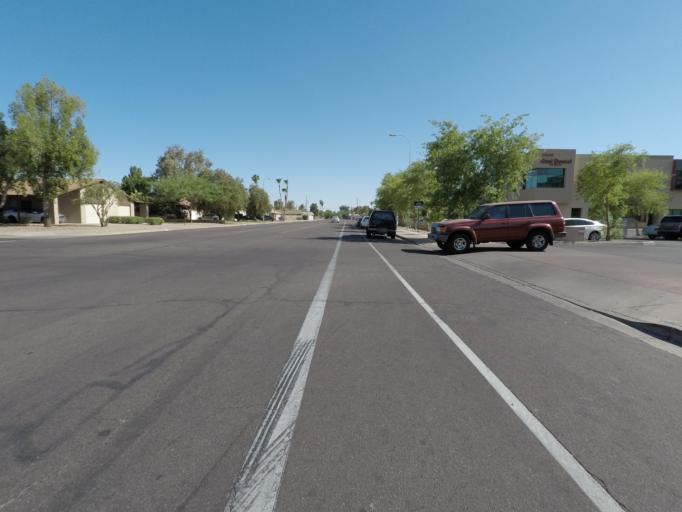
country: US
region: Arizona
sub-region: Maricopa County
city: Tempe
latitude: 33.4065
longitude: -111.9178
